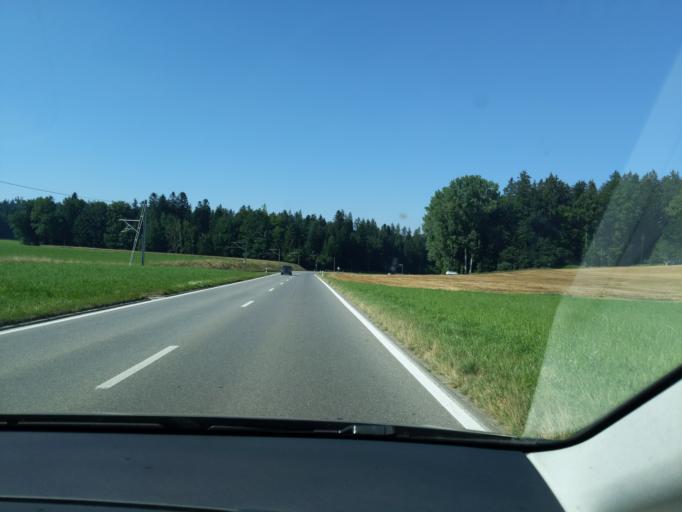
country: CH
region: Bern
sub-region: Oberaargau
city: Huttwil
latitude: 47.1175
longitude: 7.8669
